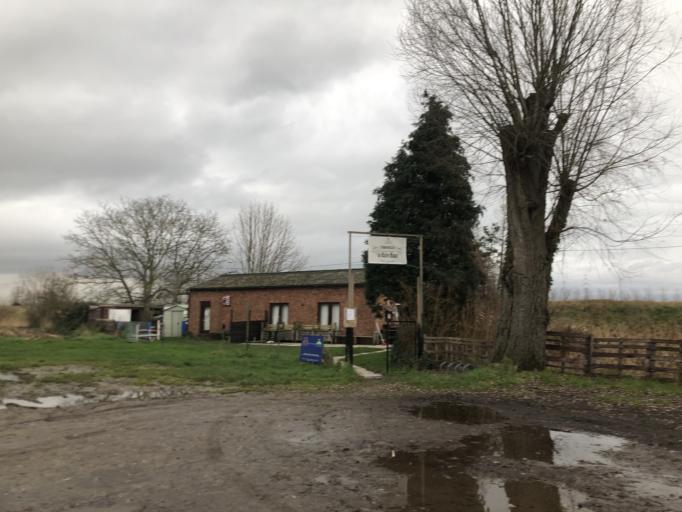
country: BE
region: Flanders
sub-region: Provincie Antwerpen
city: Zwijndrecht
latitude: 51.2318
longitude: 4.2992
